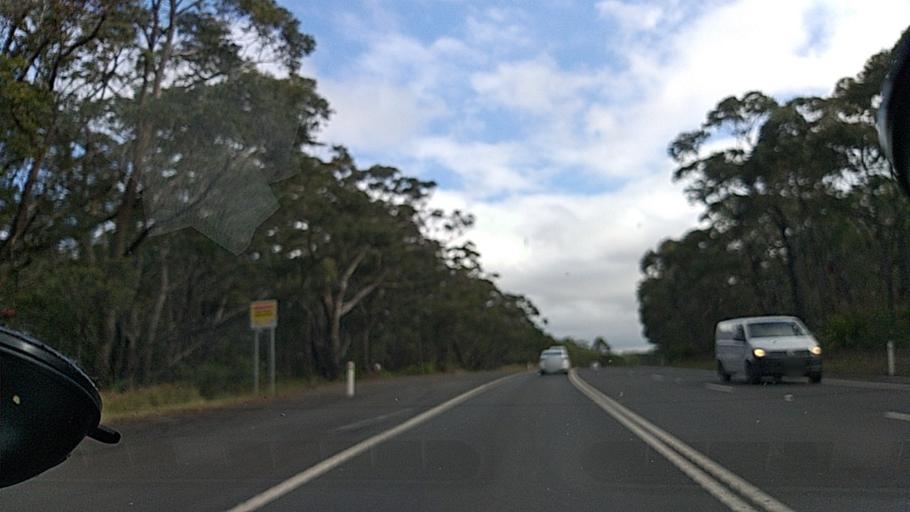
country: AU
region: New South Wales
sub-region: Wollongong
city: Bulli
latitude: -34.2728
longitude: 150.8955
